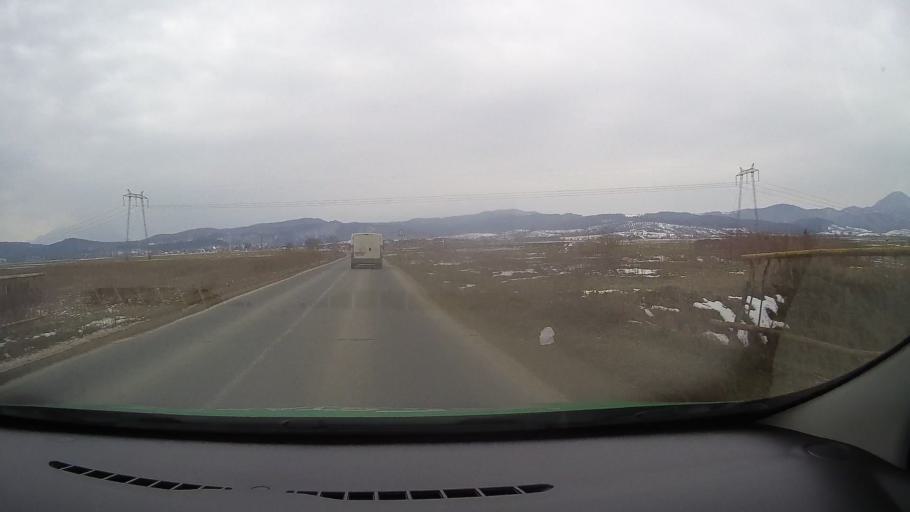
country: RO
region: Brasov
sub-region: Comuna Vulcan
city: Vulcan
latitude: 45.6364
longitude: 25.4416
